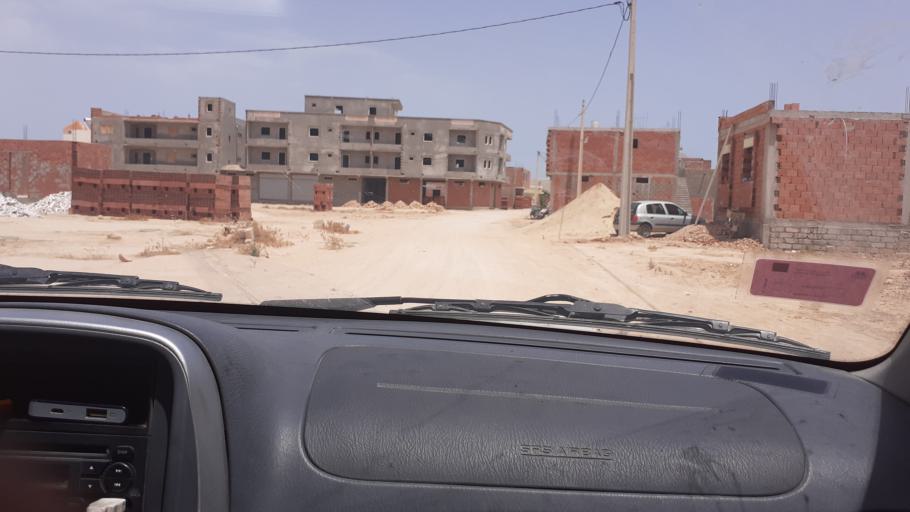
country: TN
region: Qabis
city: Matmata
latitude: 33.6103
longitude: 10.2895
